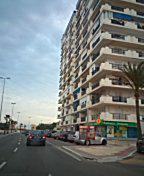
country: ES
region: Murcia
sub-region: Murcia
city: La Manga del Mar Menor
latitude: 37.6868
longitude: -0.7365
